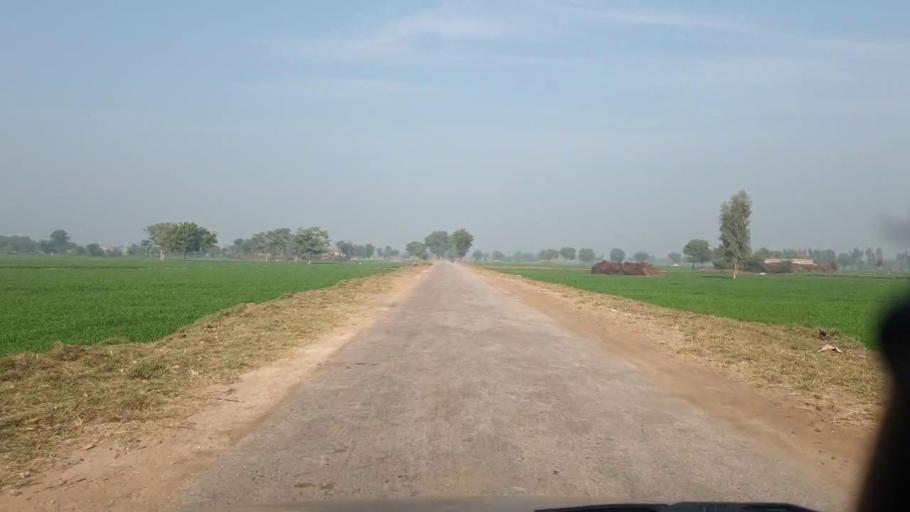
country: PK
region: Sindh
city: Shahdadpur
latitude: 26.0049
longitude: 68.5523
